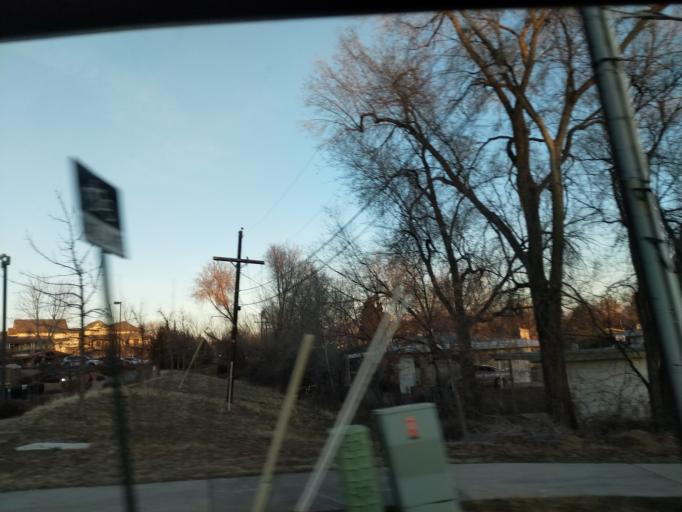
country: US
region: Colorado
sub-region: Mesa County
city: Grand Junction
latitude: 39.0946
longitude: -108.5523
